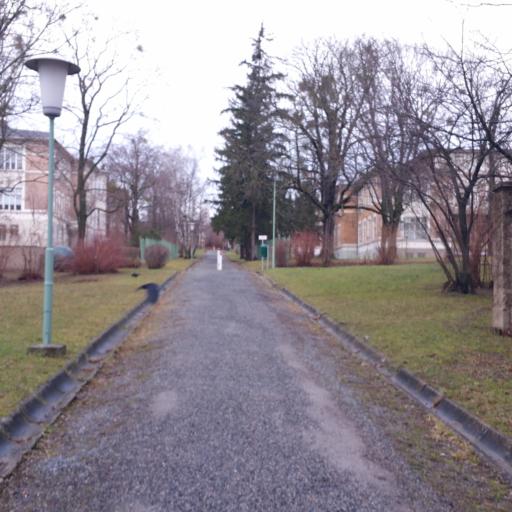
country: AT
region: Vienna
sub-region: Wien Stadt
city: Vienna
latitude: 48.2092
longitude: 16.2831
